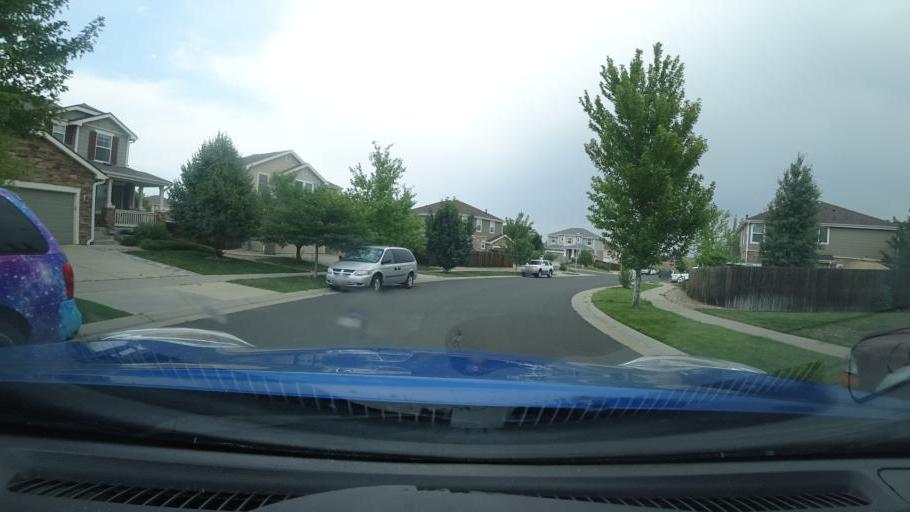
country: US
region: Colorado
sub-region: Adams County
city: Aurora
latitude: 39.6906
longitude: -104.7614
